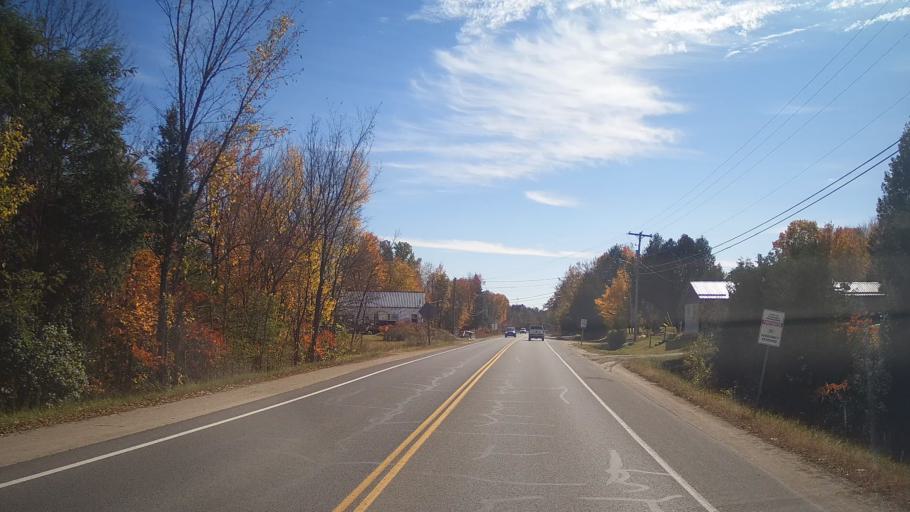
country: CA
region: Ontario
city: Perth
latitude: 44.7970
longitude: -76.6788
